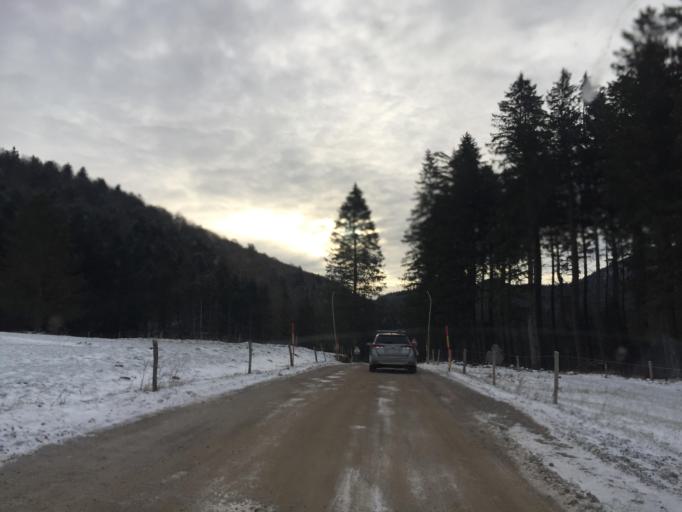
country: SI
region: Nova Gorica
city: Sempas
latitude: 46.0026
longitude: 13.8002
